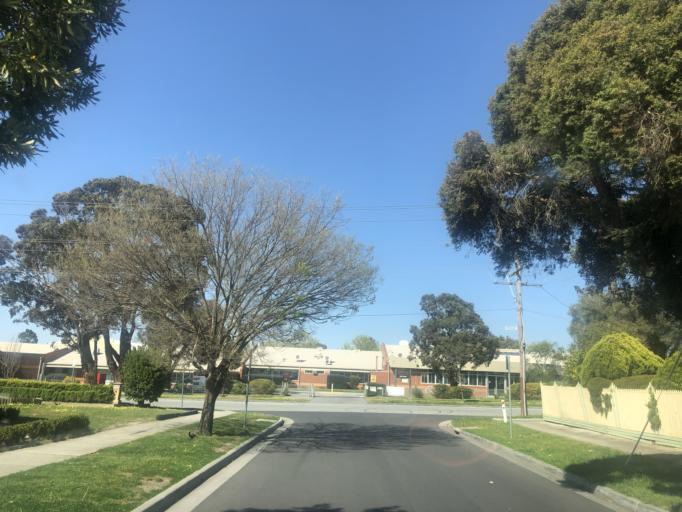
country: AU
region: Victoria
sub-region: Casey
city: Hampton Park
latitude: -38.0344
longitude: 145.2600
